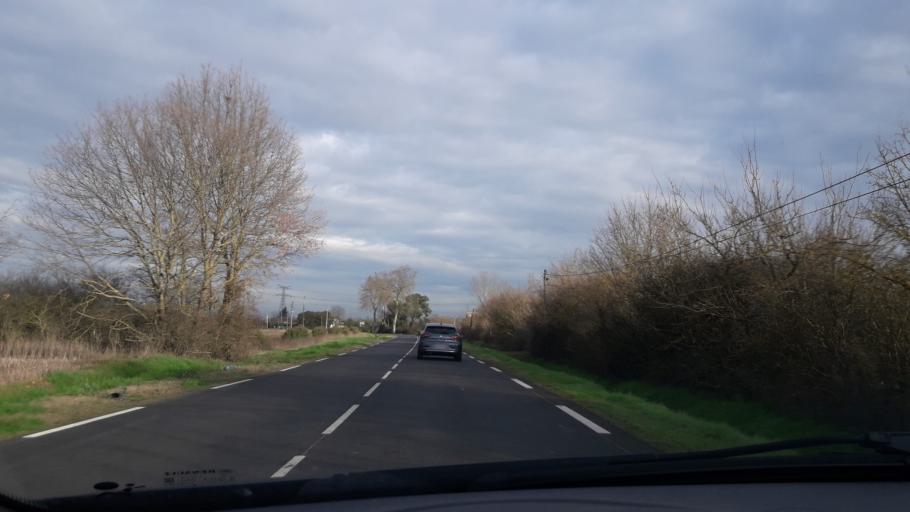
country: FR
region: Midi-Pyrenees
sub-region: Departement de la Haute-Garonne
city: Ondes
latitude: 43.7964
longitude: 1.2961
